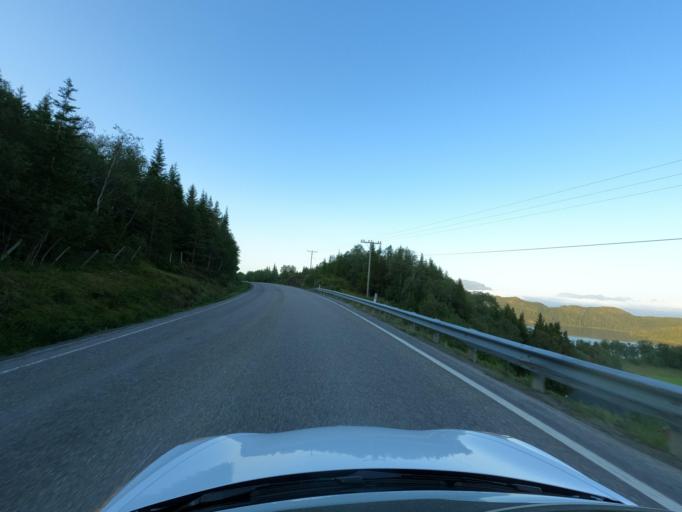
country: NO
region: Troms
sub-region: Harstad
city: Harstad
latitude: 68.7217
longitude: 16.5314
